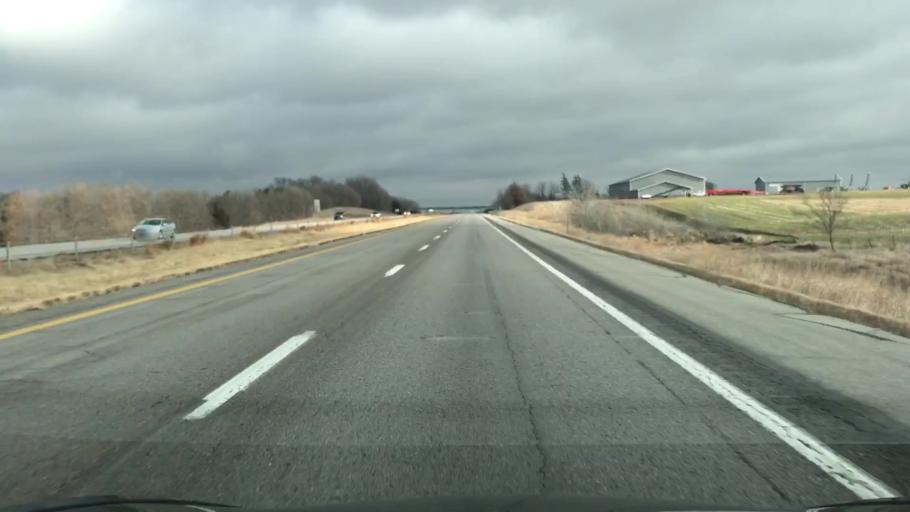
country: US
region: Iowa
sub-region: Guthrie County
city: Stuart
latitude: 41.4958
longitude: -94.4217
